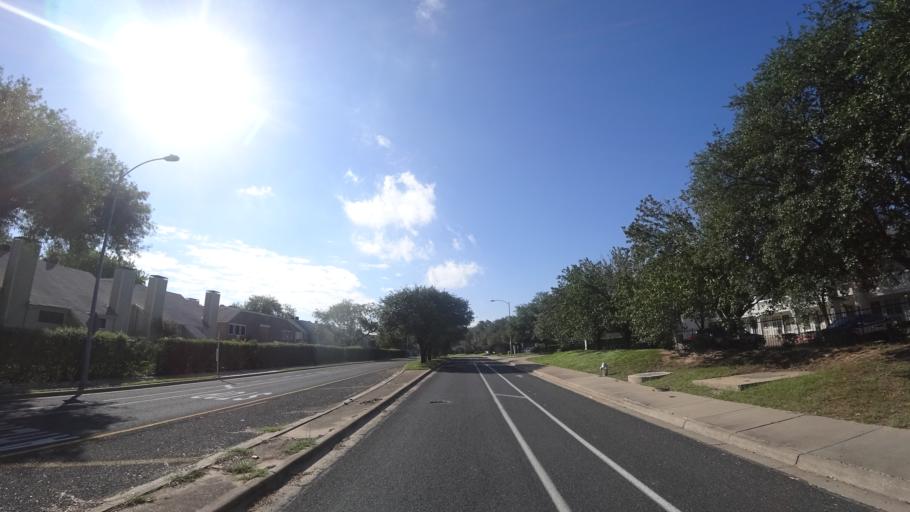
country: US
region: Texas
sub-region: Travis County
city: Austin
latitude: 30.3273
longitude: -97.7022
